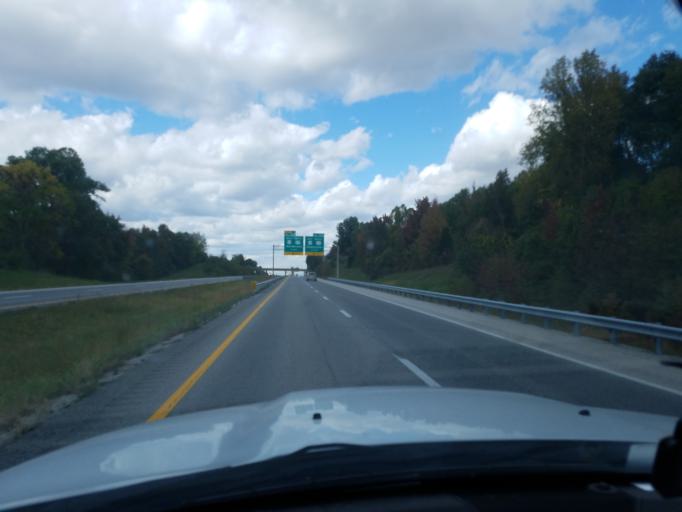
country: US
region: Kentucky
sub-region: Daviess County
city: Masonville
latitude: 37.7313
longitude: -87.0637
